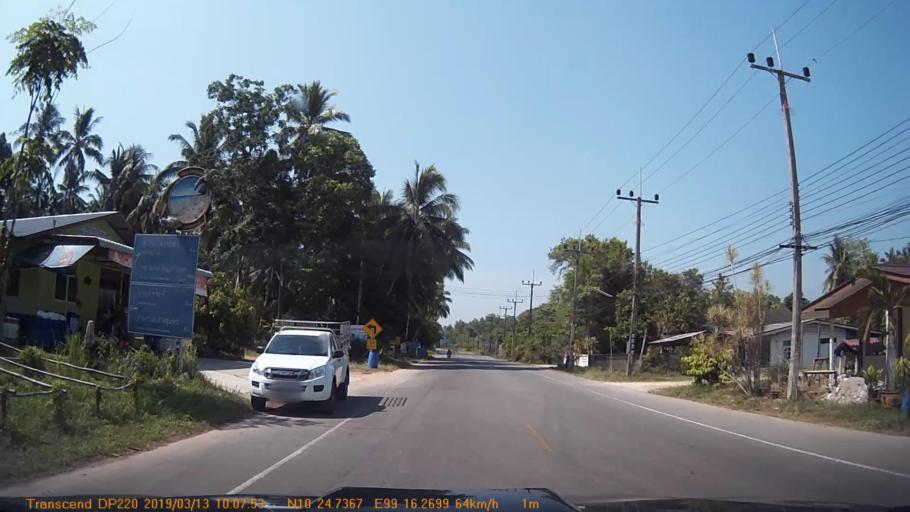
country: TH
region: Chumphon
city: Chumphon
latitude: 10.4122
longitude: 99.2711
